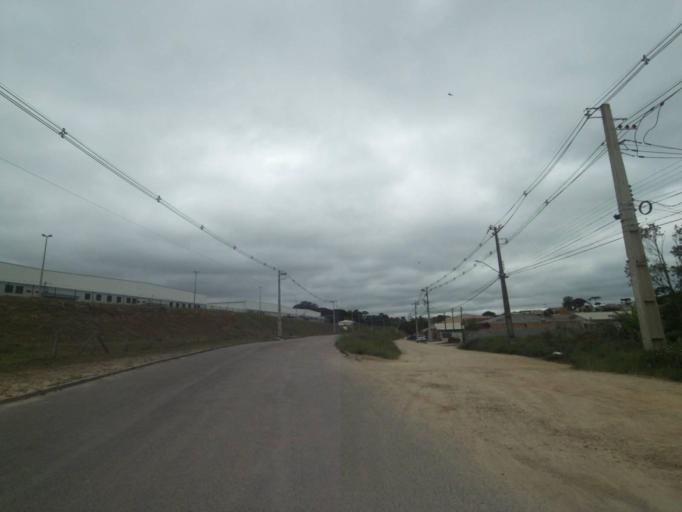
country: BR
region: Parana
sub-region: Araucaria
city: Araucaria
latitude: -25.5555
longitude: -49.3178
